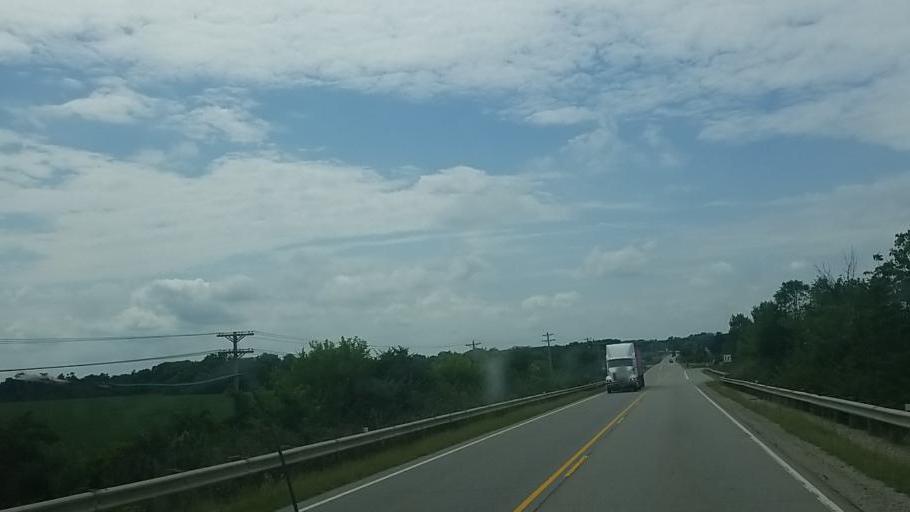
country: US
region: Ohio
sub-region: Franklin County
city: Obetz
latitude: 39.8314
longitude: -82.9576
